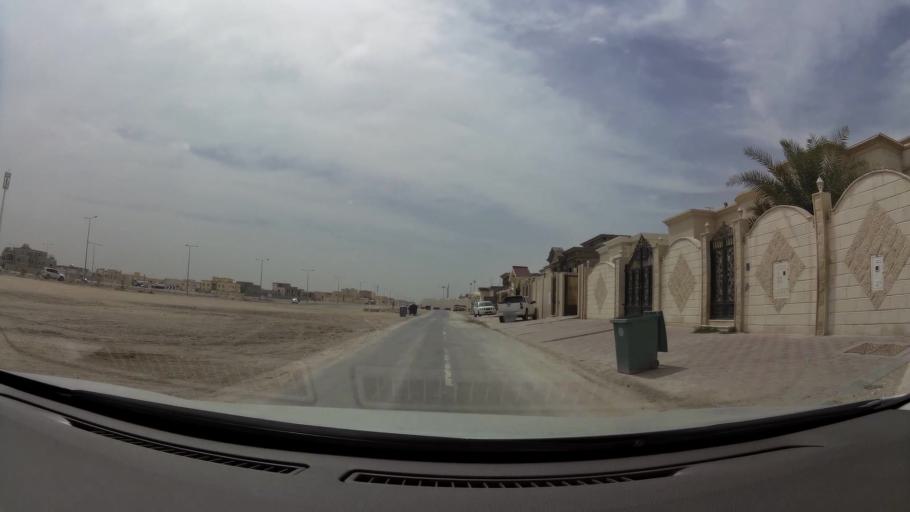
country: QA
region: Baladiyat ad Dawhah
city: Doha
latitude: 25.2154
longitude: 51.4679
